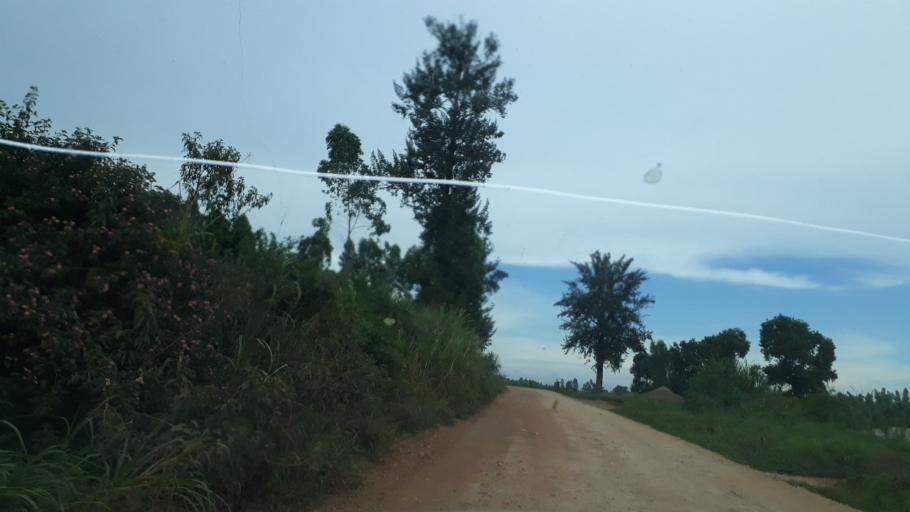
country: CD
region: Eastern Province
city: Bunia
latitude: 1.9148
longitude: 30.5031
